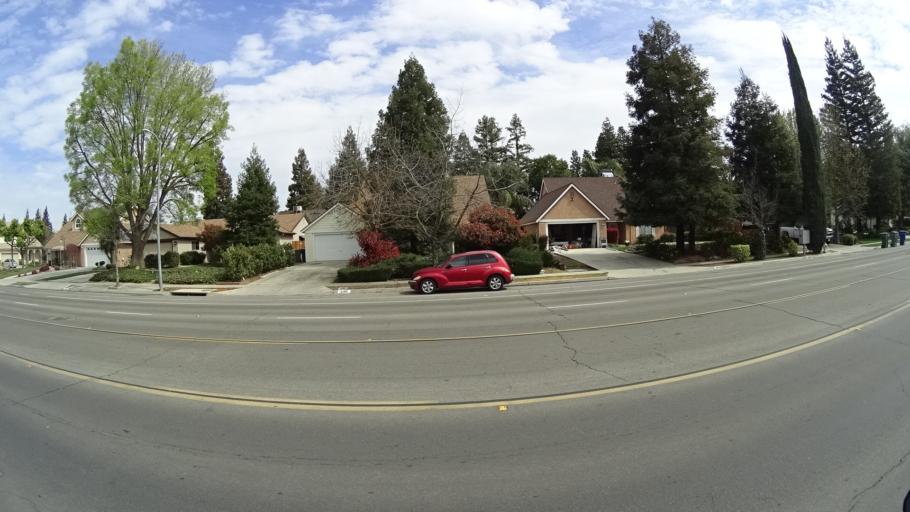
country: US
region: California
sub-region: Fresno County
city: West Park
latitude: 36.8258
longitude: -119.8746
